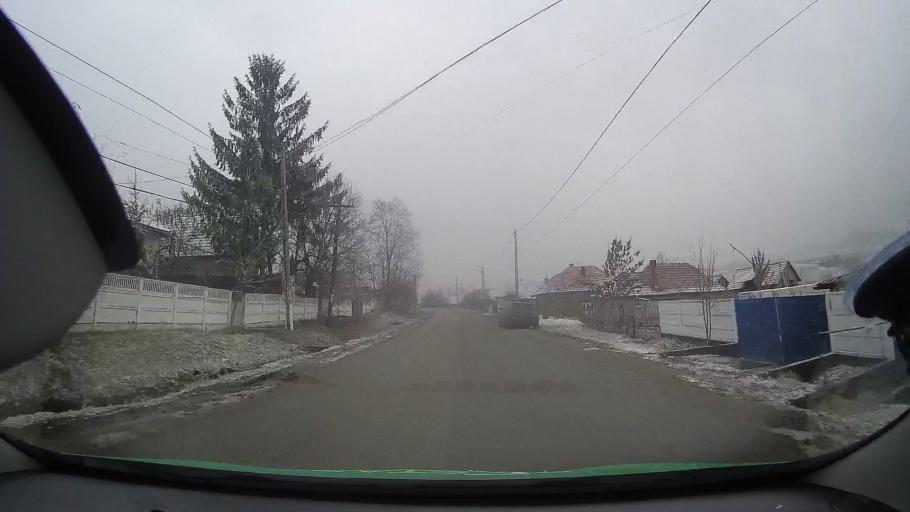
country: RO
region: Alba
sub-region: Comuna Noslac
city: Noslac
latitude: 46.3471
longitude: 23.9397
